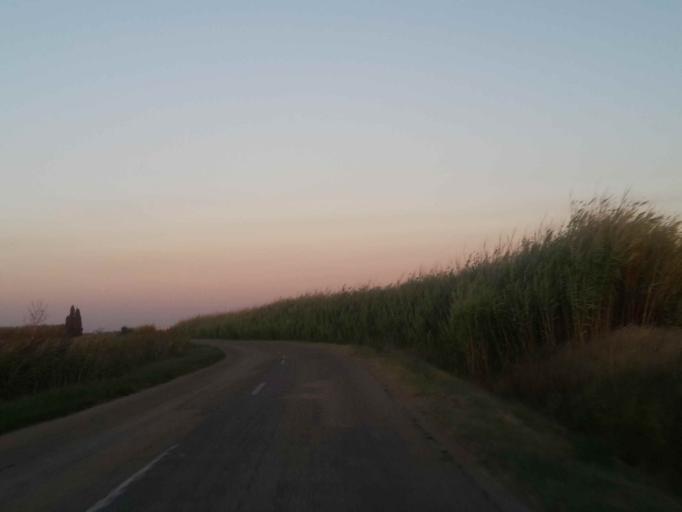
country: FR
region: Provence-Alpes-Cote d'Azur
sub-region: Departement des Bouches-du-Rhone
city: Port-Saint-Louis-du-Rhone
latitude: 43.4279
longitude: 4.7014
